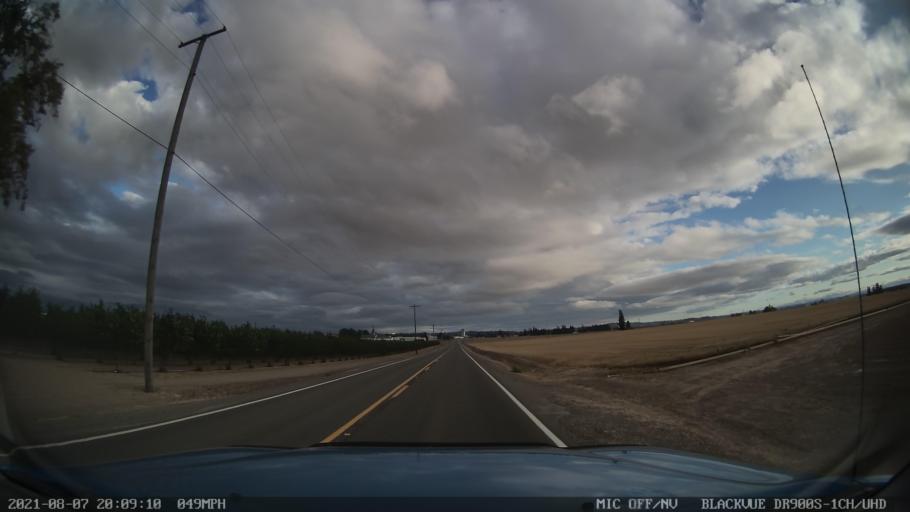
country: US
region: Oregon
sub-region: Marion County
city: Silverton
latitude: 44.9744
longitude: -122.8776
